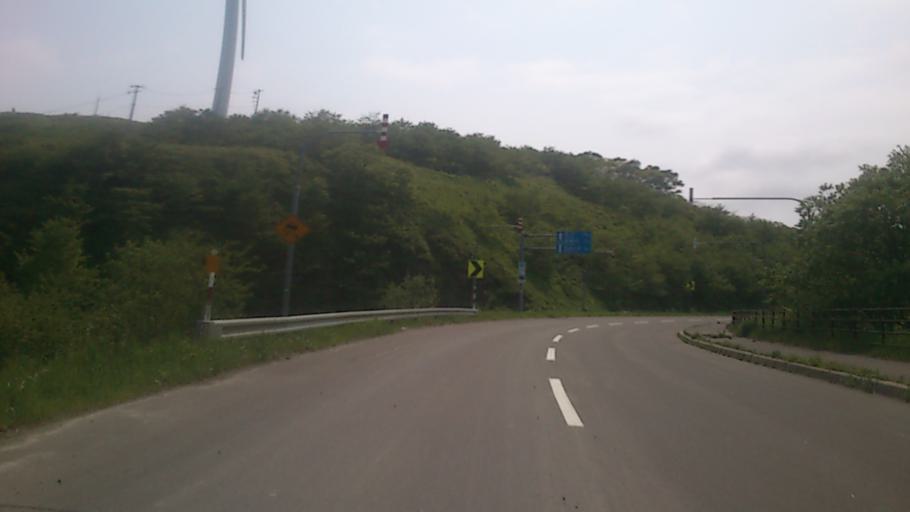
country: JP
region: Hokkaido
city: Nemuro
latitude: 43.2788
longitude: 145.5620
